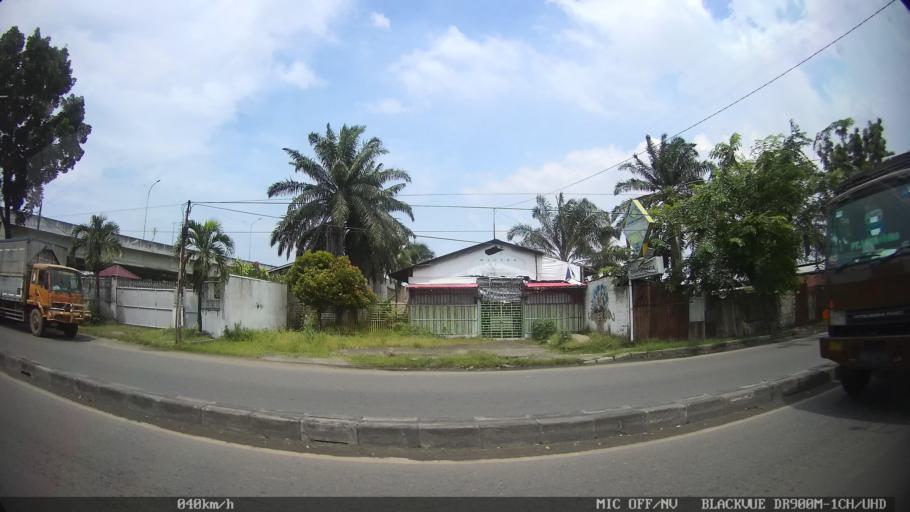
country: ID
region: North Sumatra
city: Medan
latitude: 3.6471
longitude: 98.6629
